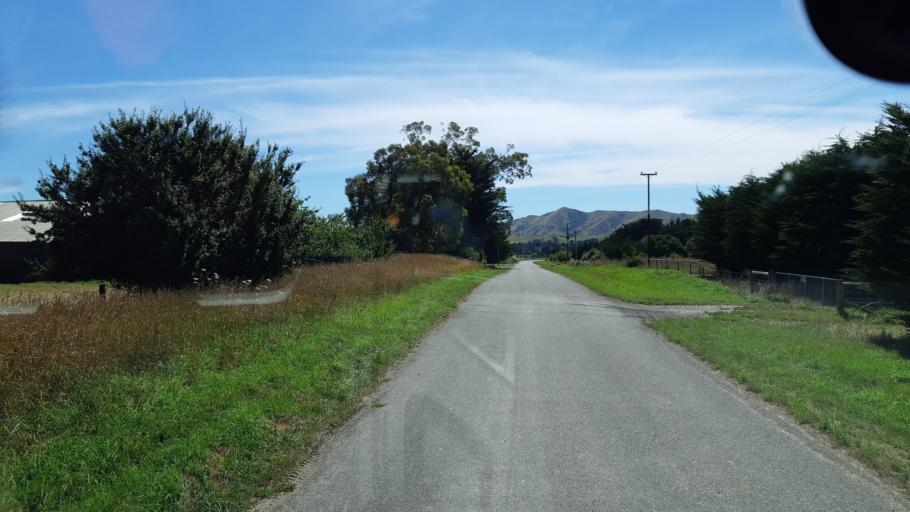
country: NZ
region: Marlborough
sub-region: Marlborough District
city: Blenheim
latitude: -41.8310
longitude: 174.1053
